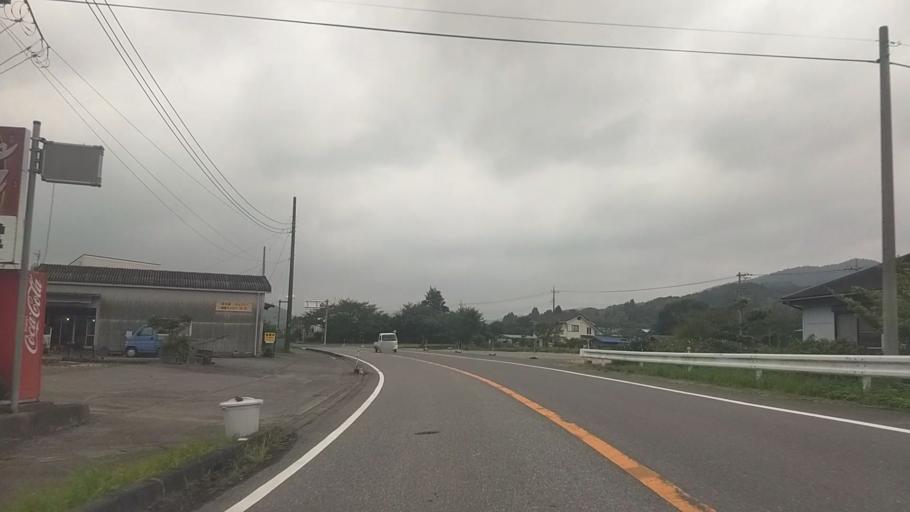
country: JP
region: Chiba
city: Kawaguchi
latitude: 35.1379
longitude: 139.9888
